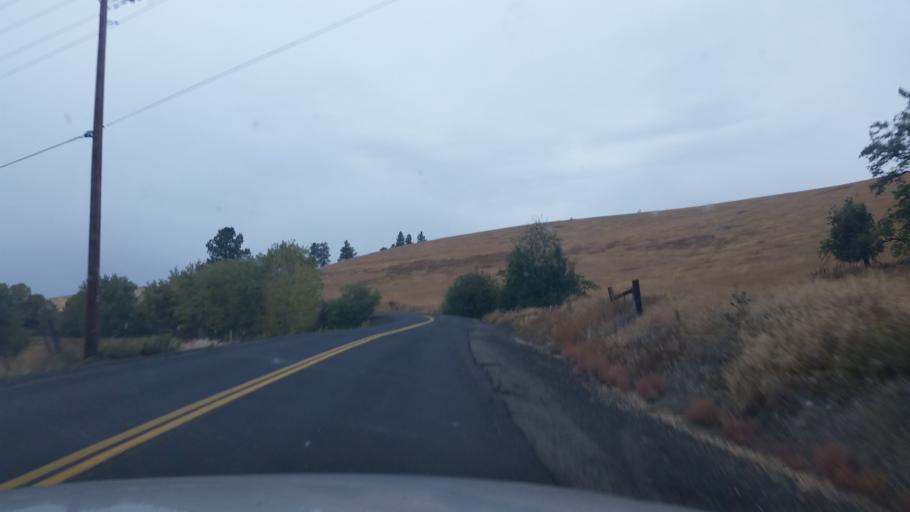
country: US
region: Washington
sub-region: Spokane County
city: Cheney
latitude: 47.5382
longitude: -117.5479
